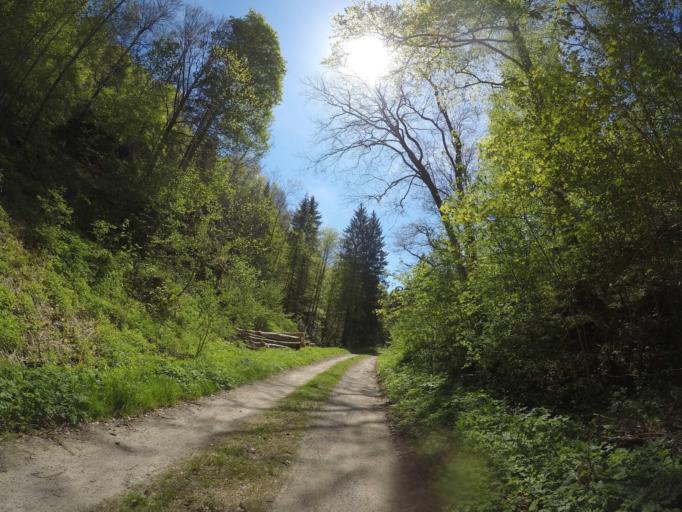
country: DE
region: Baden-Wuerttemberg
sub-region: Tuebingen Region
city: Schelklingen
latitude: 48.4194
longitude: 9.7078
